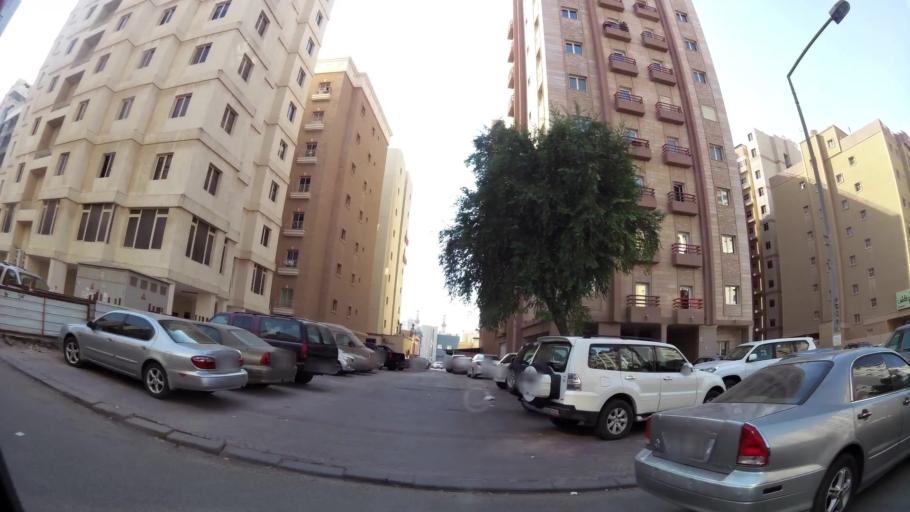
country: KW
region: Muhafazat Hawalli
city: As Salimiyah
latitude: 29.3427
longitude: 48.0936
